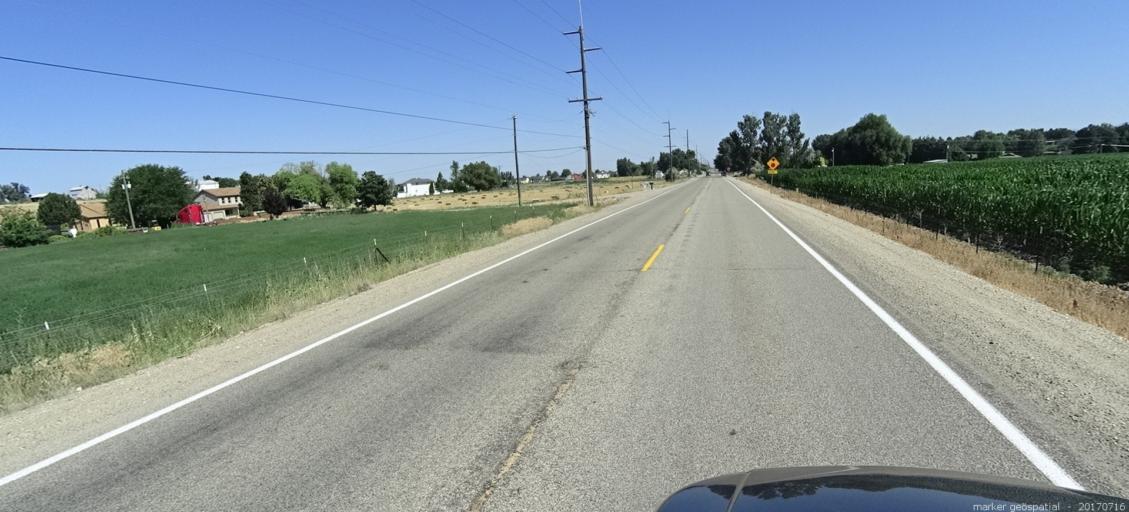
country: US
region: Idaho
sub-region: Ada County
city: Kuna
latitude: 43.5297
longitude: -116.3344
